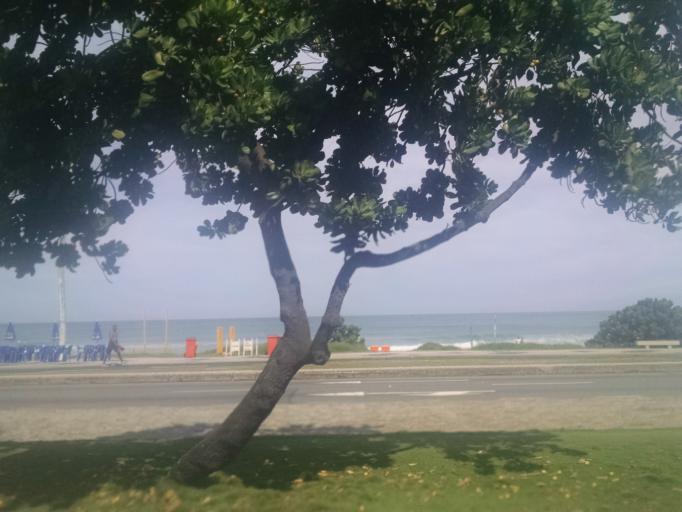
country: BR
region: Rio de Janeiro
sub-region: Rio De Janeiro
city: Rio de Janeiro
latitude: -23.0102
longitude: -43.3497
